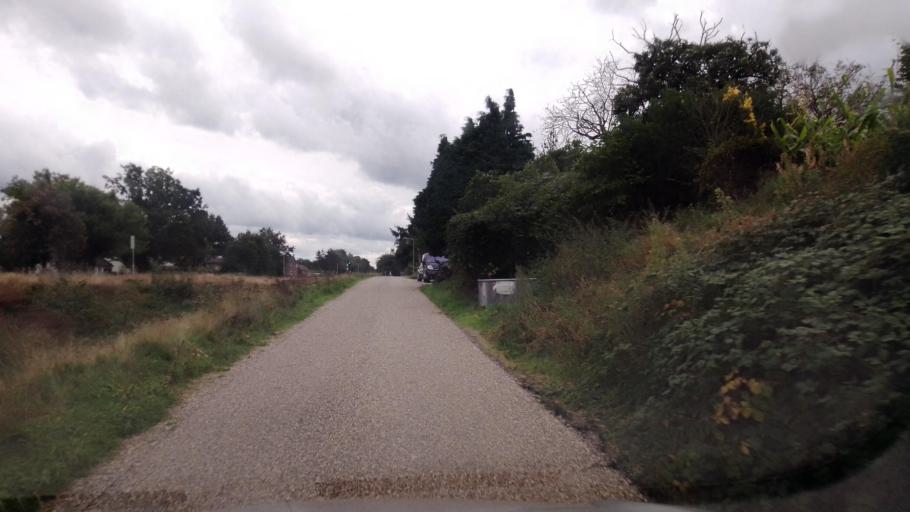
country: NL
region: Limburg
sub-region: Gemeente Venlo
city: Venlo
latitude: 51.4247
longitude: 6.1338
